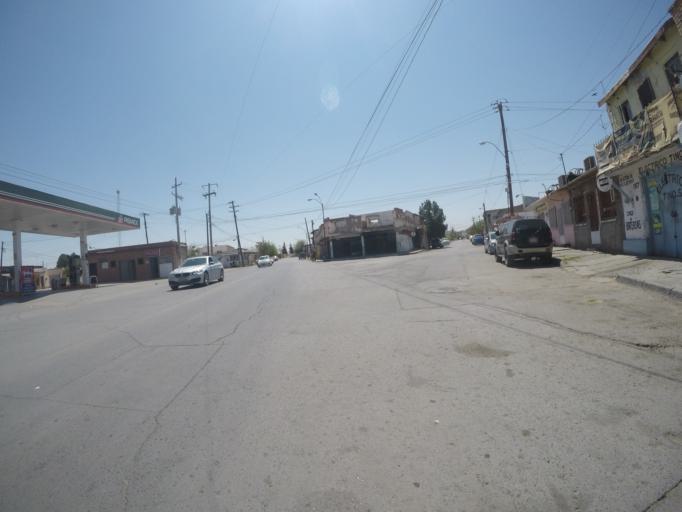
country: MX
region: Chihuahua
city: Ciudad Juarez
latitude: 31.7242
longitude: -106.4825
